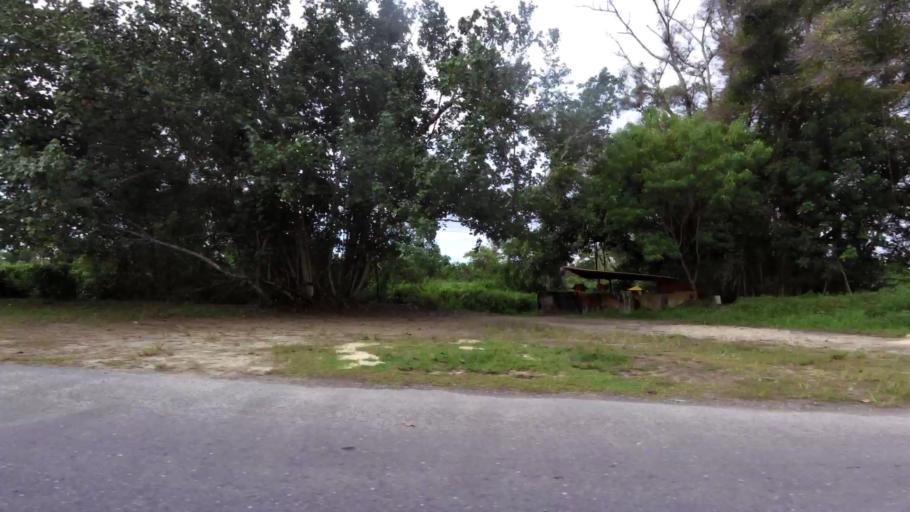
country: BN
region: Belait
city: Seria
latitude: 4.6143
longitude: 114.3487
